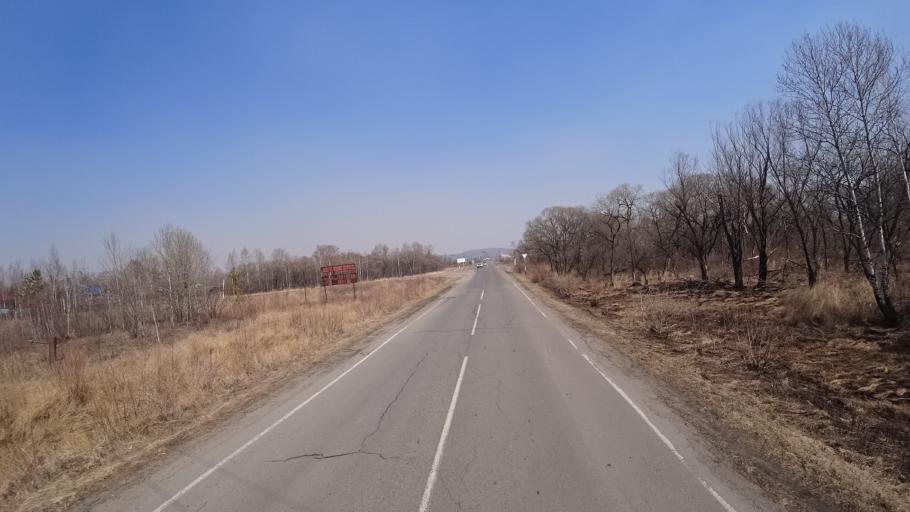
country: RU
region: Amur
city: Novobureyskiy
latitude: 49.7893
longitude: 129.8490
